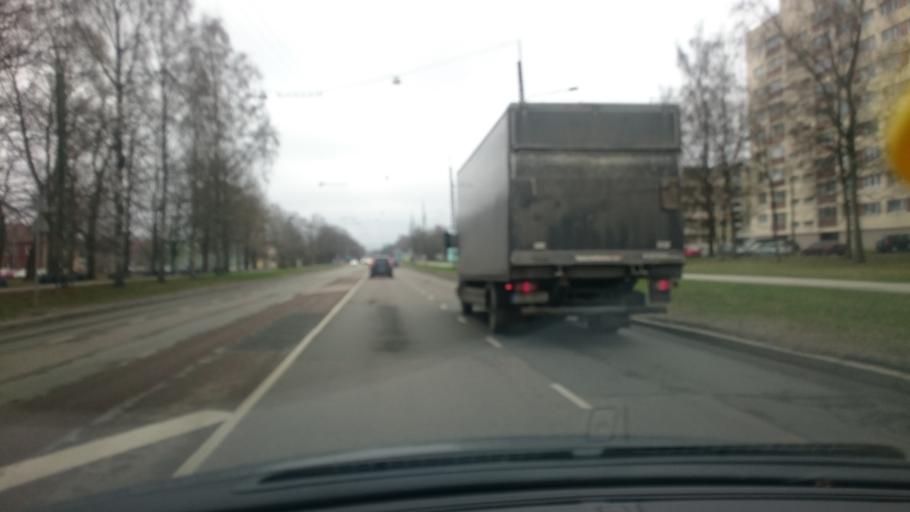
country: EE
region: Harju
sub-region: Tallinna linn
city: Tallinn
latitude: 59.4419
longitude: 24.7055
